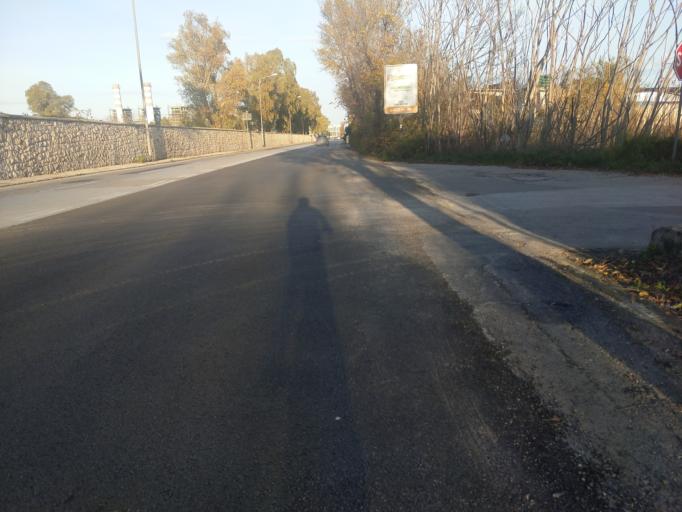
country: IT
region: Apulia
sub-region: Provincia di Bari
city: Bari
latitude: 41.1129
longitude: 16.8310
